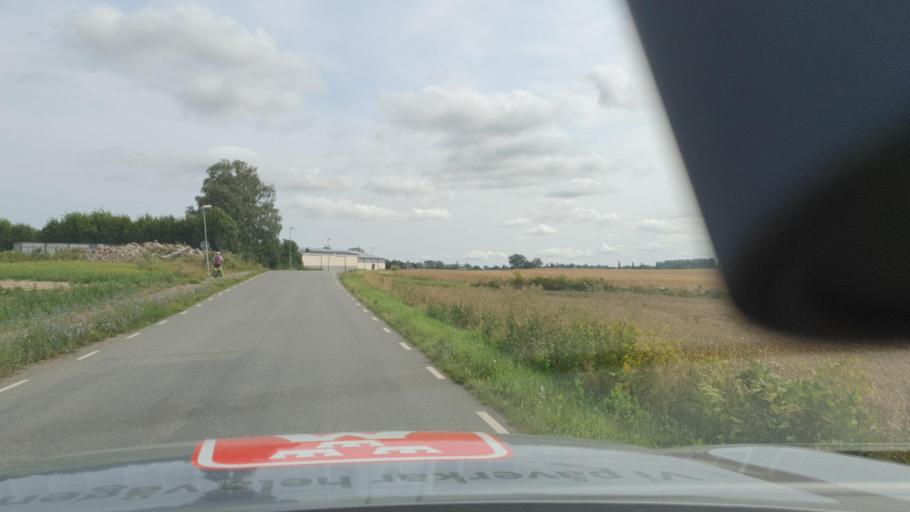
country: SE
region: Skane
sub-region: Kristianstads Kommun
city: Fjalkinge
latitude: 56.0385
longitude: 14.2495
